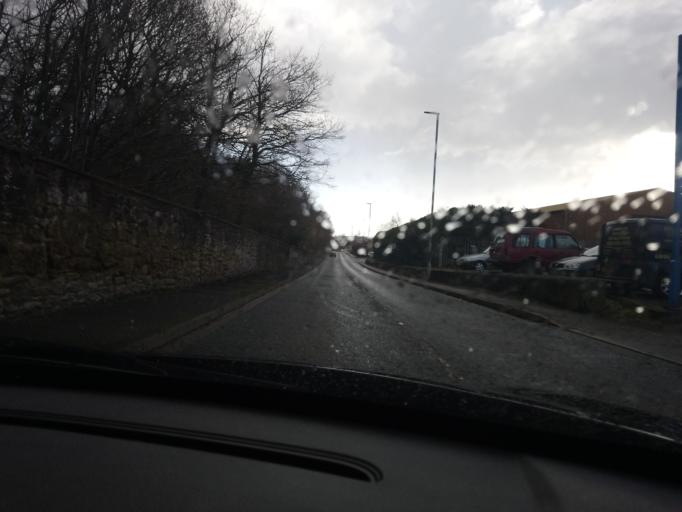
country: GB
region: Wales
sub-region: Wrexham
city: Ruabon
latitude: 52.9723
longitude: -3.0676
